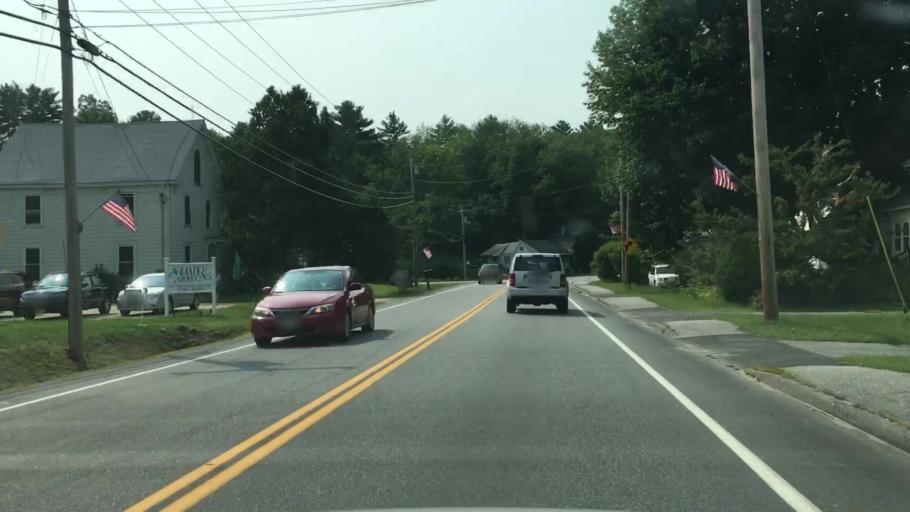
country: US
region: Maine
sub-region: Oxford County
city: Buckfield
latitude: 44.2863
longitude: -70.3583
